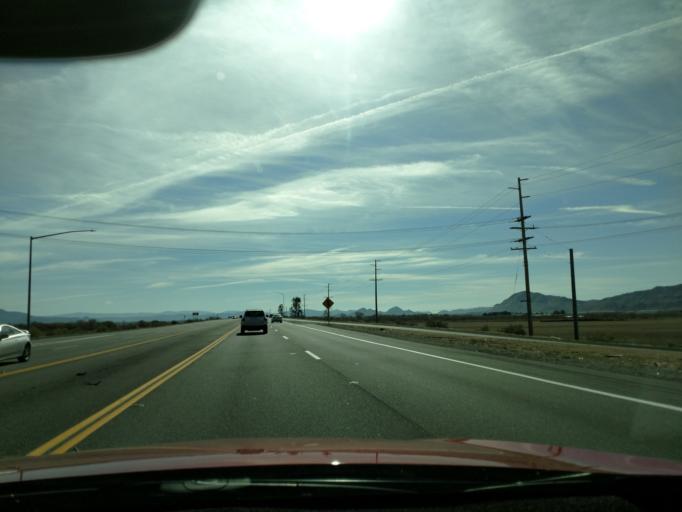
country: US
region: California
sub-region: Riverside County
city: San Jacinto
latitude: 33.8418
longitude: -117.0036
